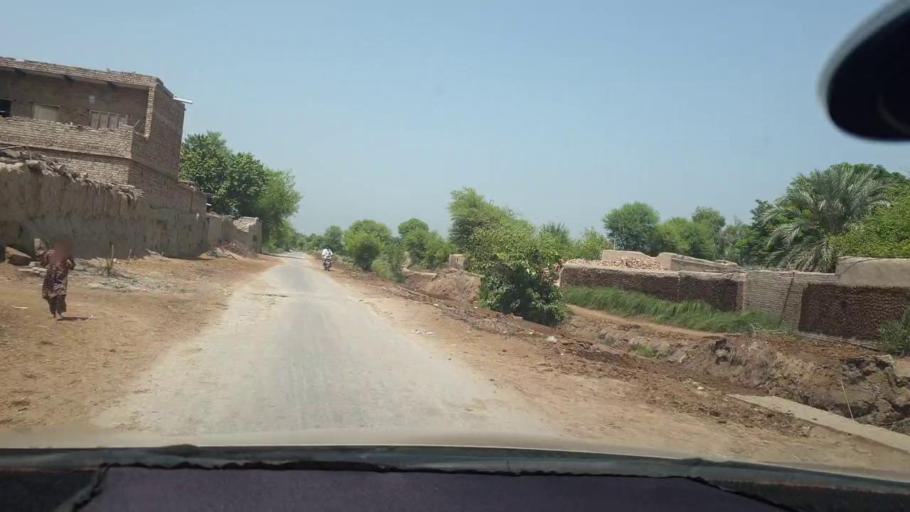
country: PK
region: Sindh
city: Kambar
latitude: 27.6503
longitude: 67.9667
